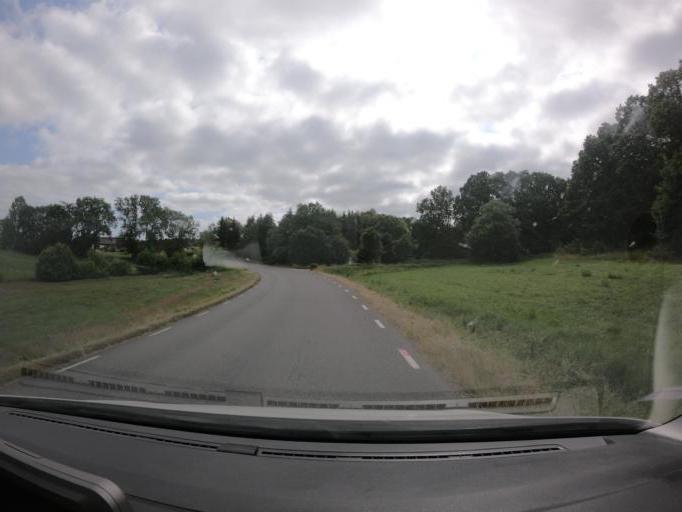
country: SE
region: Skane
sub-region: Hassleholms Kommun
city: Tormestorp
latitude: 56.1491
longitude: 13.6284
